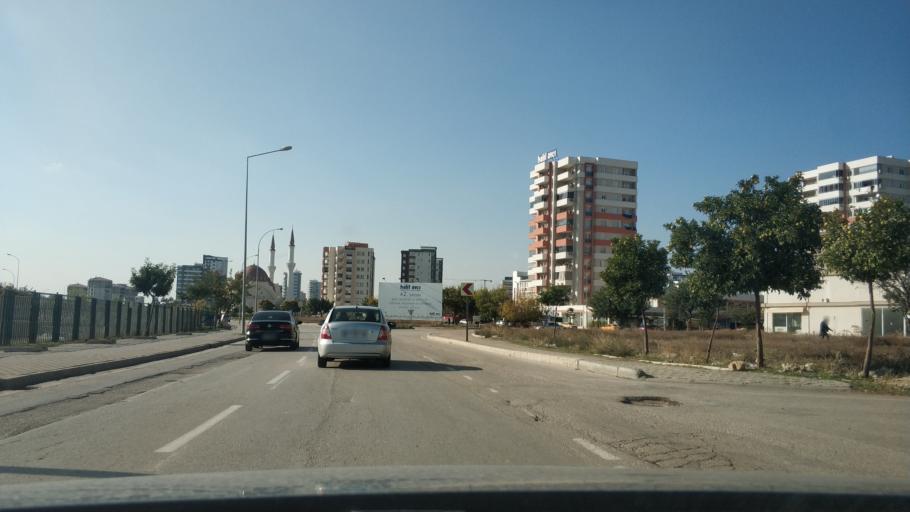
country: TR
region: Adana
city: Seyhan
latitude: 37.0099
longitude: 35.2657
